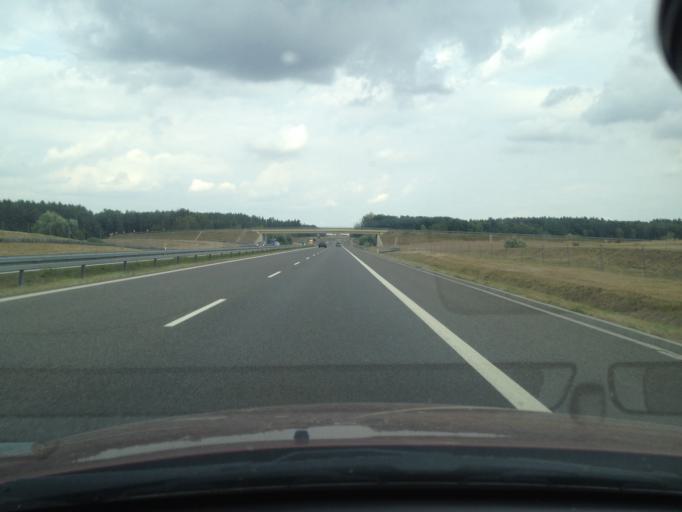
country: PL
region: West Pomeranian Voivodeship
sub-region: Powiat mysliborski
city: Mysliborz
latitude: 53.0048
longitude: 14.8620
